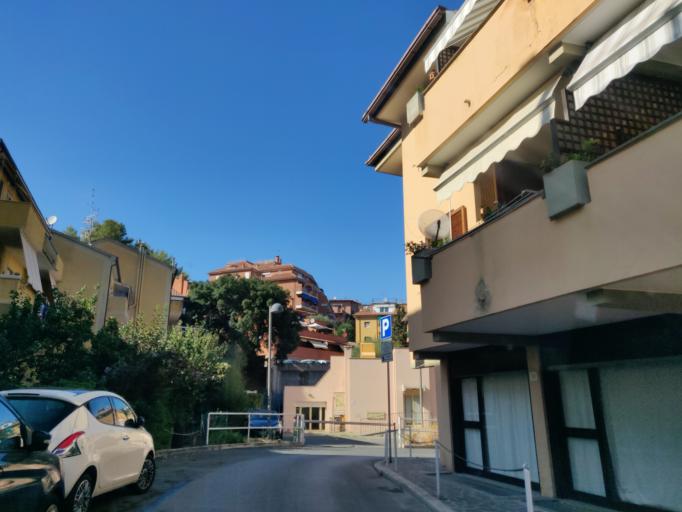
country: IT
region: Tuscany
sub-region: Provincia di Grosseto
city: Porto Ercole
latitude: 42.3927
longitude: 11.2025
